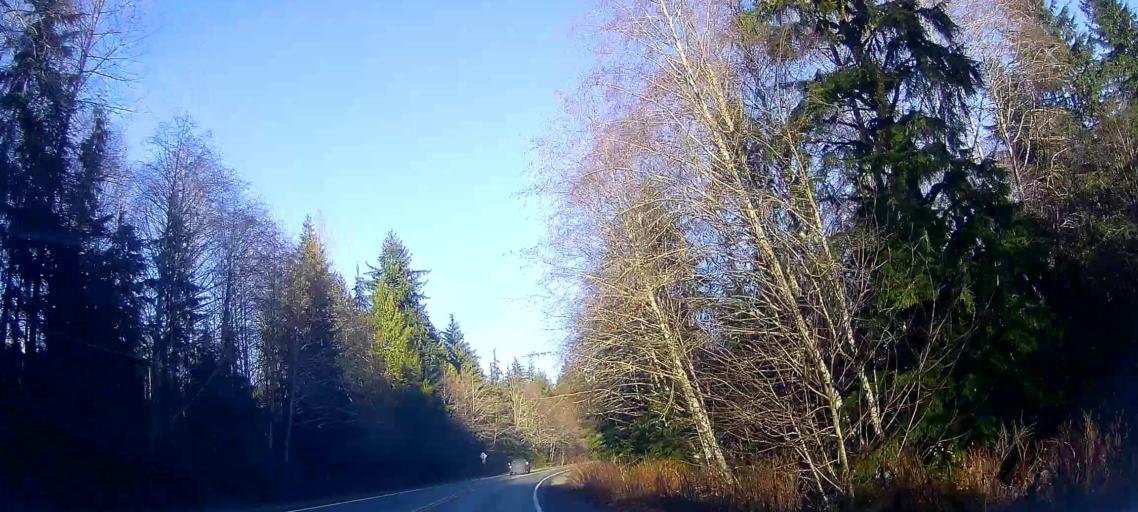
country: US
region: Washington
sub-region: Snohomish County
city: Darrington
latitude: 48.6393
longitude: -121.7346
